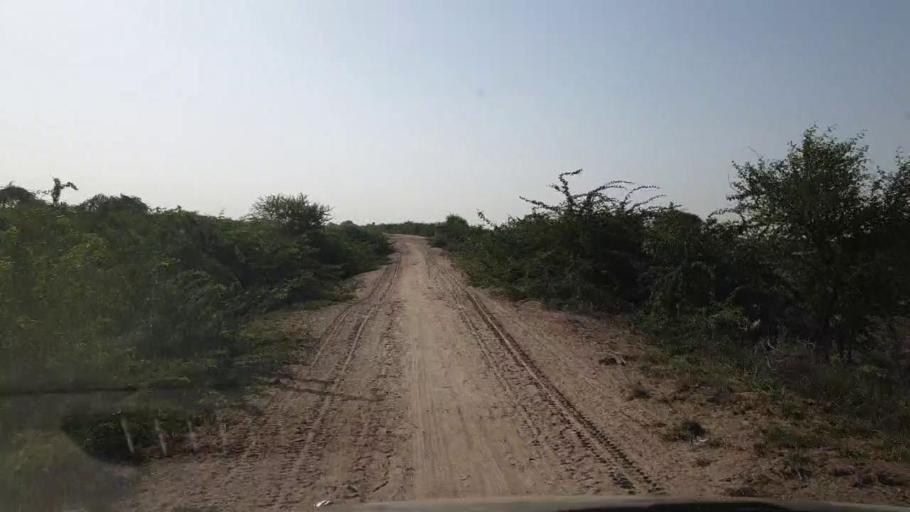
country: PK
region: Sindh
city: Kadhan
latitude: 24.5936
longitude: 69.0760
